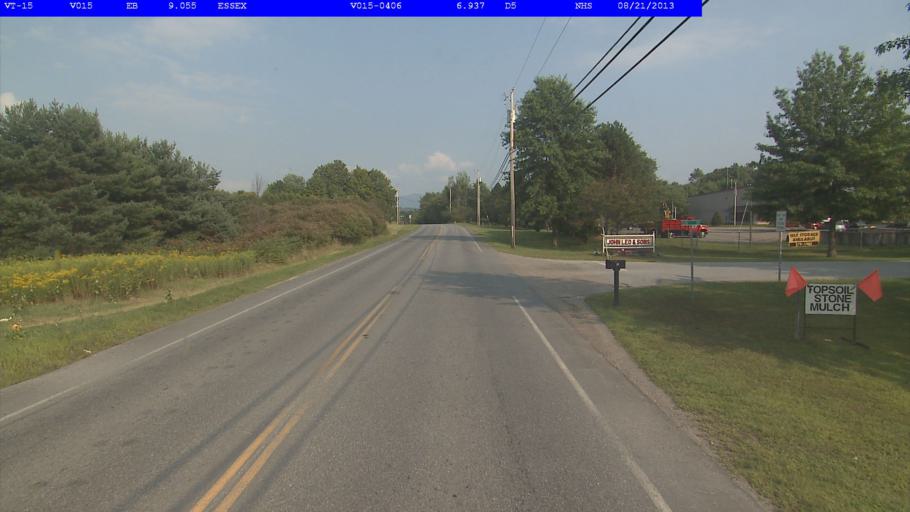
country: US
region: Vermont
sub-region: Chittenden County
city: Jericho
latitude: 44.5025
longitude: -73.0309
